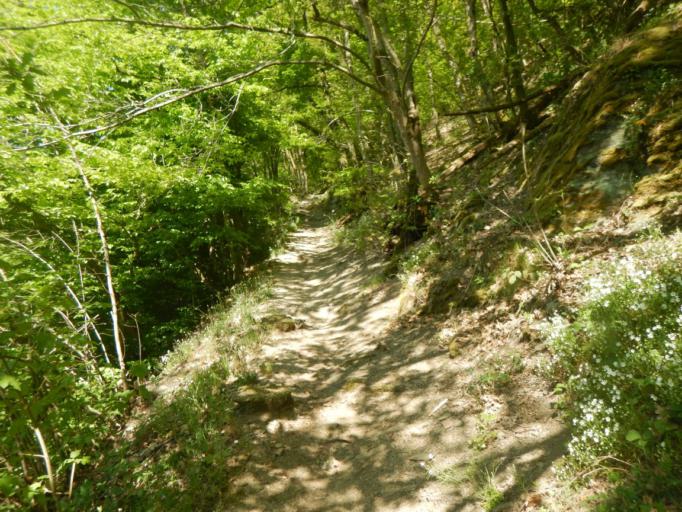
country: LU
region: Diekirch
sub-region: Canton de Diekirch
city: Bourscheid
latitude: 49.9143
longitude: 6.0877
